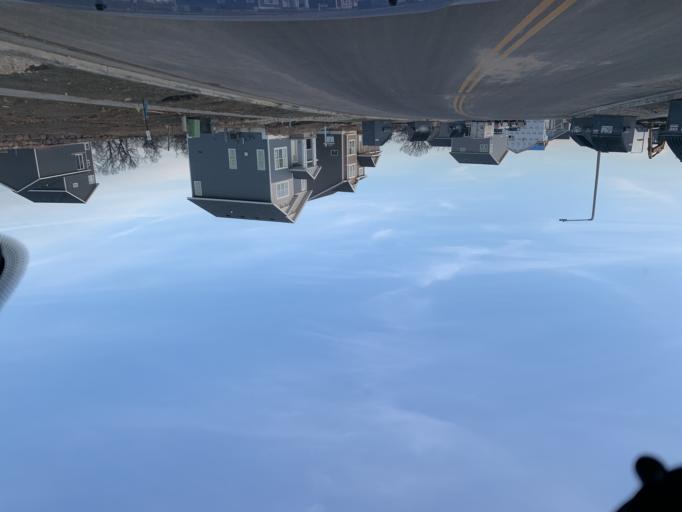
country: US
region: Wisconsin
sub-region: Dane County
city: Verona
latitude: 43.0462
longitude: -89.5572
